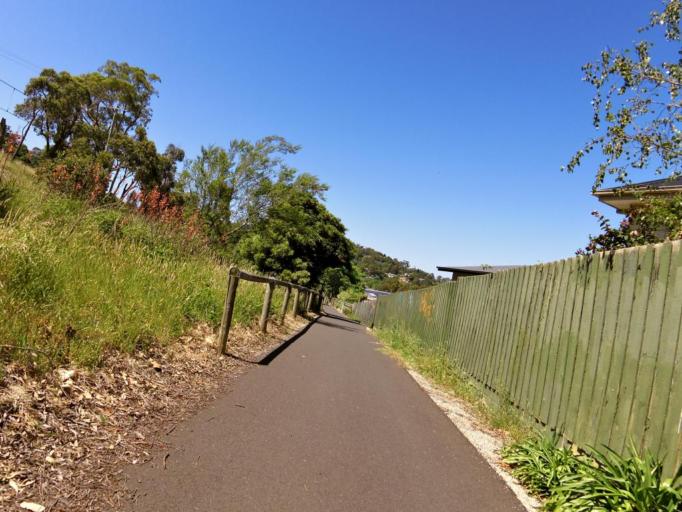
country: AU
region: Victoria
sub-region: Knox
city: Ferntree Gully
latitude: -37.8883
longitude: 145.2985
